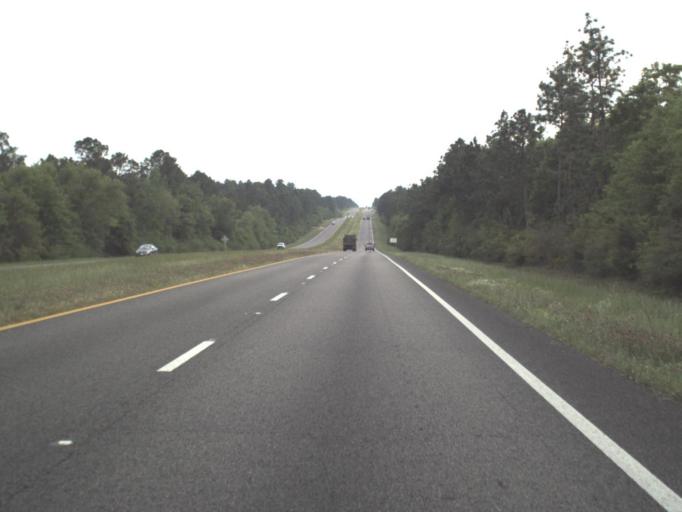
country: US
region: Florida
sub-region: Escambia County
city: Molino
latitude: 30.6936
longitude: -87.3509
